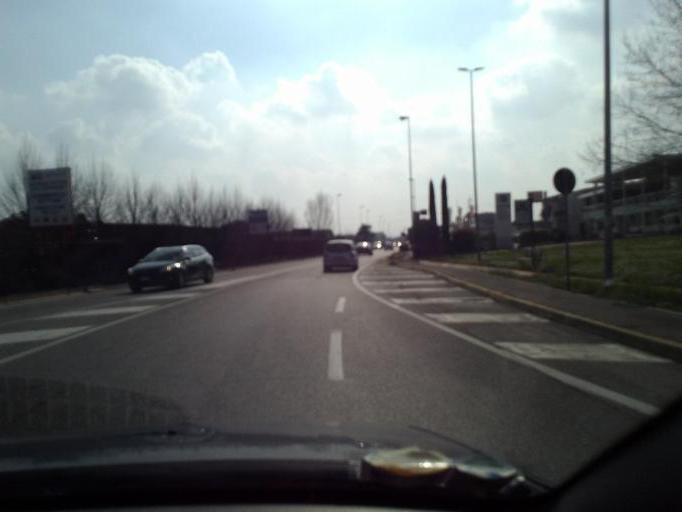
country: IT
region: Veneto
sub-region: Provincia di Verona
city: Villafranca di Verona
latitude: 45.3651
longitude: 10.8626
